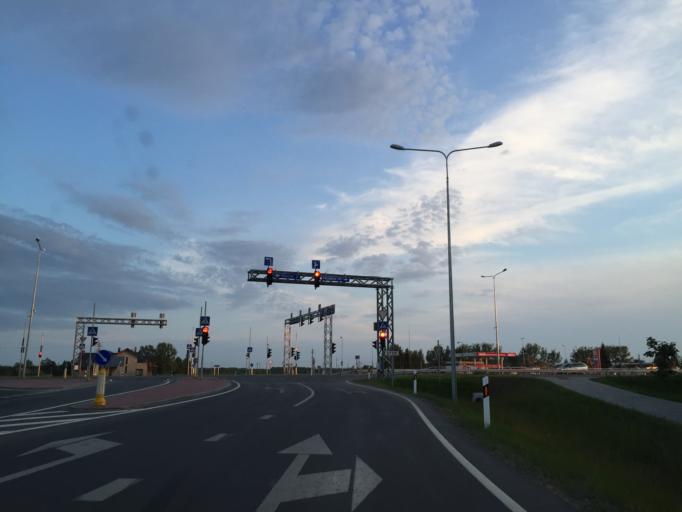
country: LT
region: Siauliu apskritis
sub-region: Siauliai
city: Siauliai
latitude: 55.9801
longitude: 23.1381
